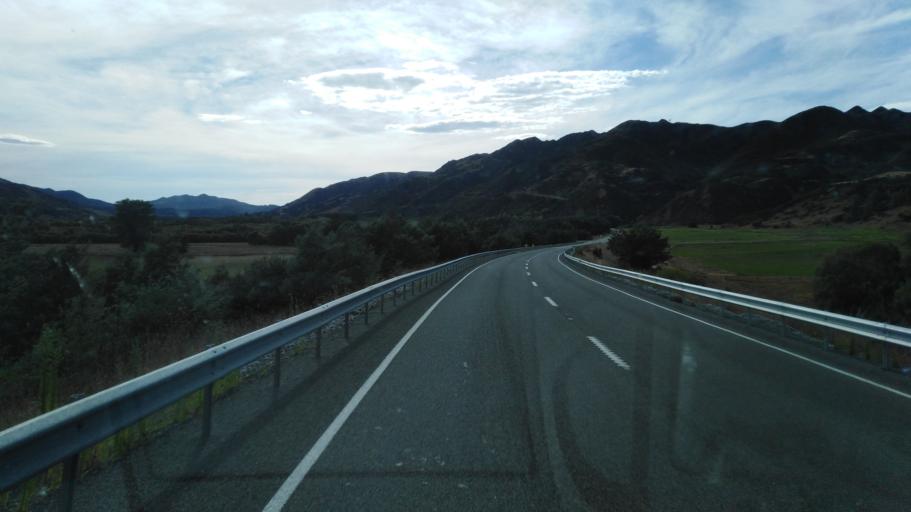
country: NZ
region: Canterbury
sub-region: Kaikoura District
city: Kaikoura
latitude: -42.6369
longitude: 173.3295
